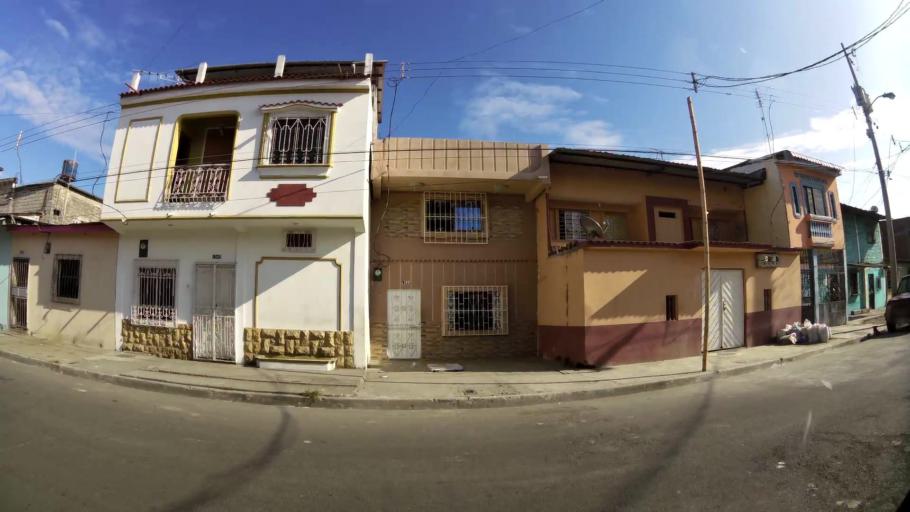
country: EC
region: Guayas
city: Guayaquil
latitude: -2.2101
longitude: -79.9245
